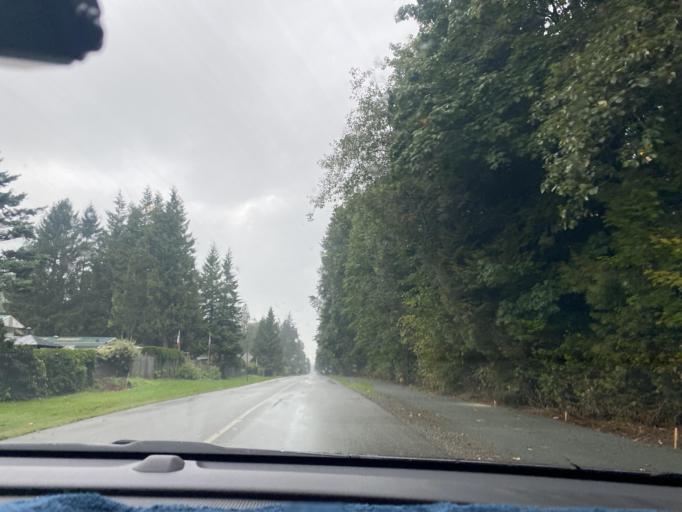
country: CA
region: British Columbia
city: Agassiz
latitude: 49.2807
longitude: -121.7775
